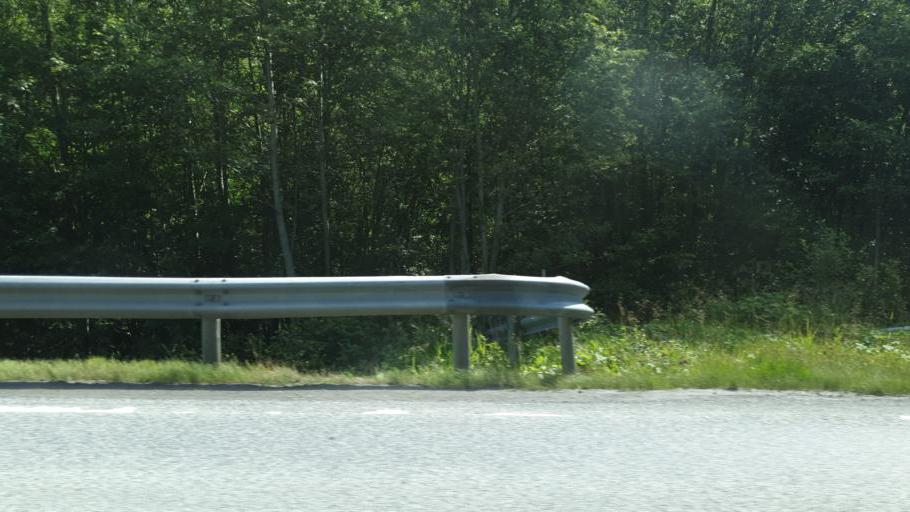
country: NO
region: Sor-Trondelag
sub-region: Midtre Gauldal
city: Storen
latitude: 63.0062
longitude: 10.2397
